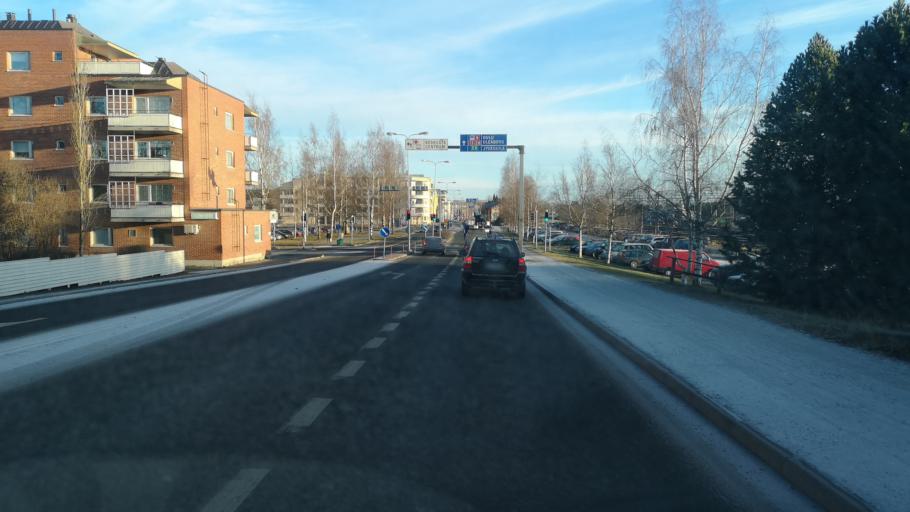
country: FI
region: Central Ostrobothnia
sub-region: Kokkola
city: Kokkola
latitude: 63.8347
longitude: 23.1252
